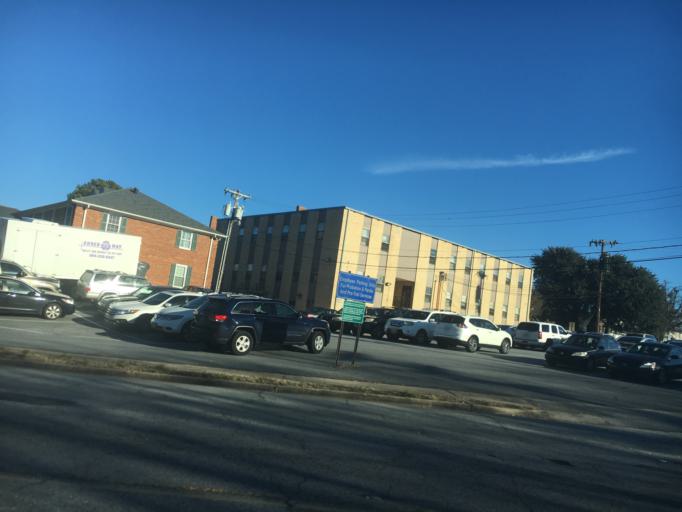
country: US
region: South Carolina
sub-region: Spartanburg County
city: Spartanburg
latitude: 34.9527
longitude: -81.9370
